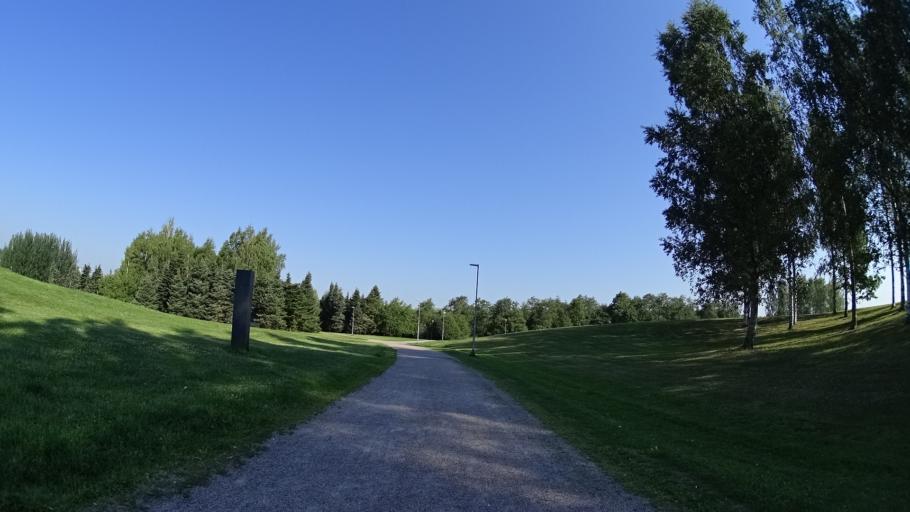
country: FI
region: Uusimaa
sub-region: Helsinki
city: Vantaa
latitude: 60.2780
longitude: 24.9850
